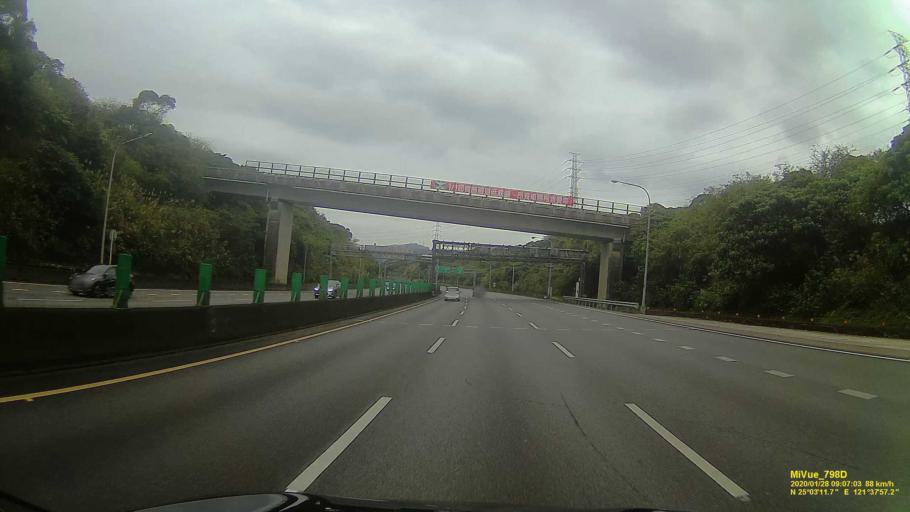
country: TW
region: Taipei
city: Taipei
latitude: 25.0533
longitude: 121.6317
